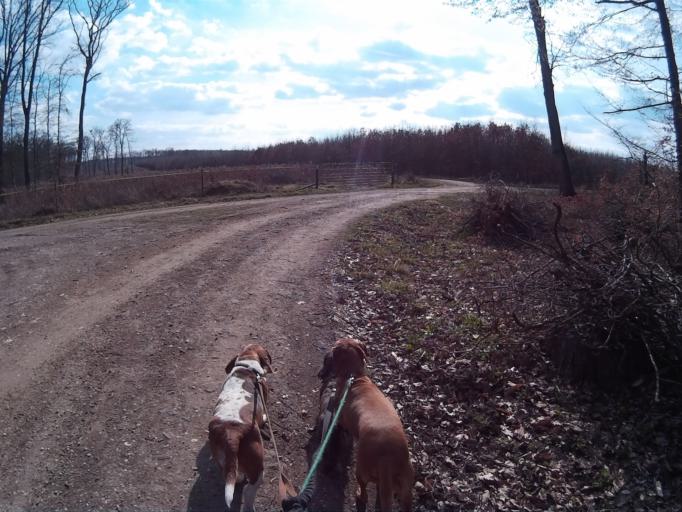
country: HU
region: Vas
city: Sarvar
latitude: 47.1983
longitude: 16.9975
